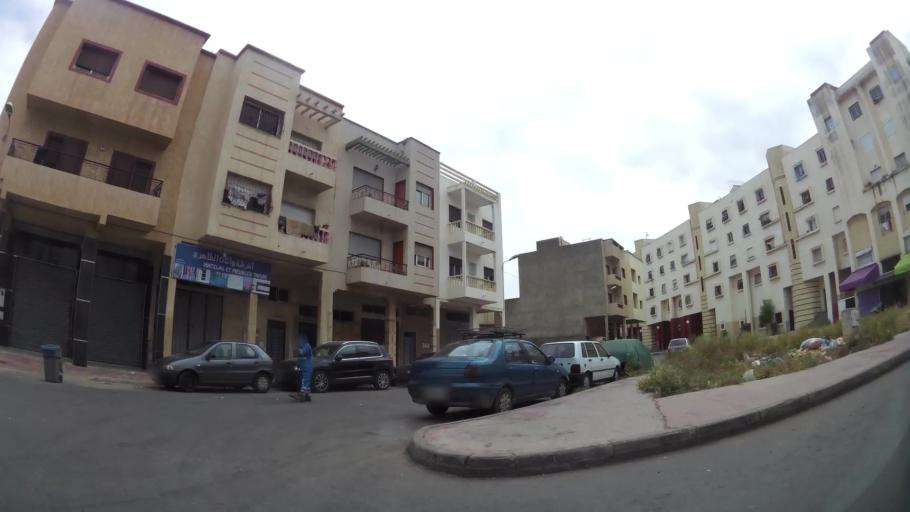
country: MA
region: Rabat-Sale-Zemmour-Zaer
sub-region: Rabat
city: Rabat
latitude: 33.9957
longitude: -6.8772
